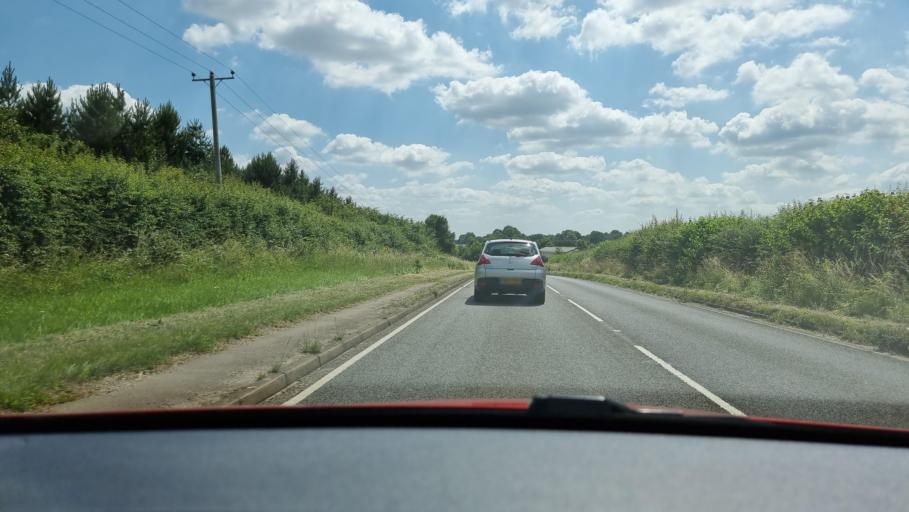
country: GB
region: England
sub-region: Oxfordshire
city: Kidlington
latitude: 51.8411
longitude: -1.3089
